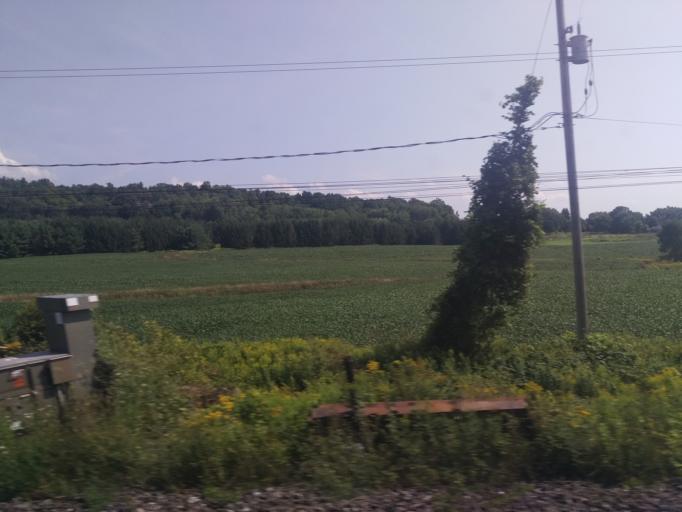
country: CA
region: Ontario
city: Brockville
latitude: 44.5804
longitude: -75.7270
